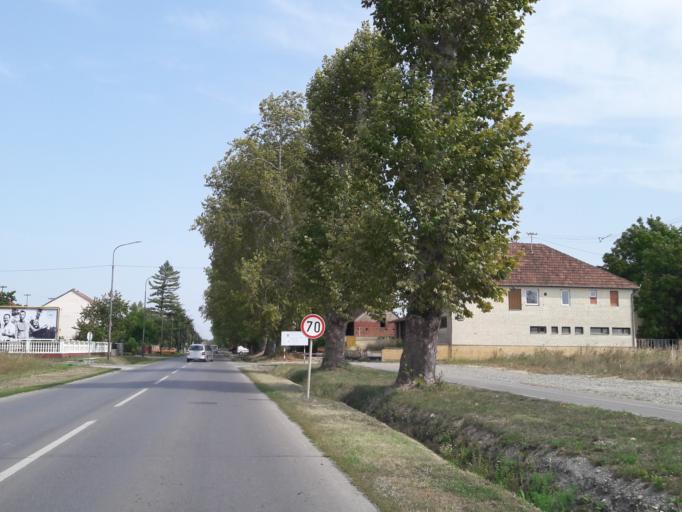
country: HR
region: Osjecko-Baranjska
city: Cepin
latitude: 45.5283
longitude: 18.6043
